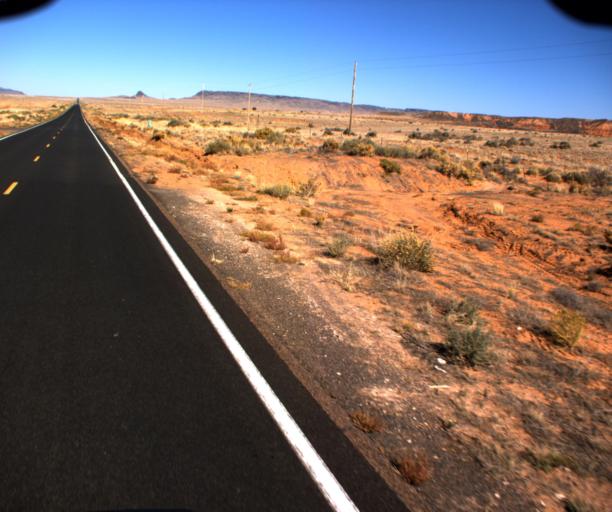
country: US
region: Arizona
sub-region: Navajo County
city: Dilkon
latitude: 35.3304
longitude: -110.4235
